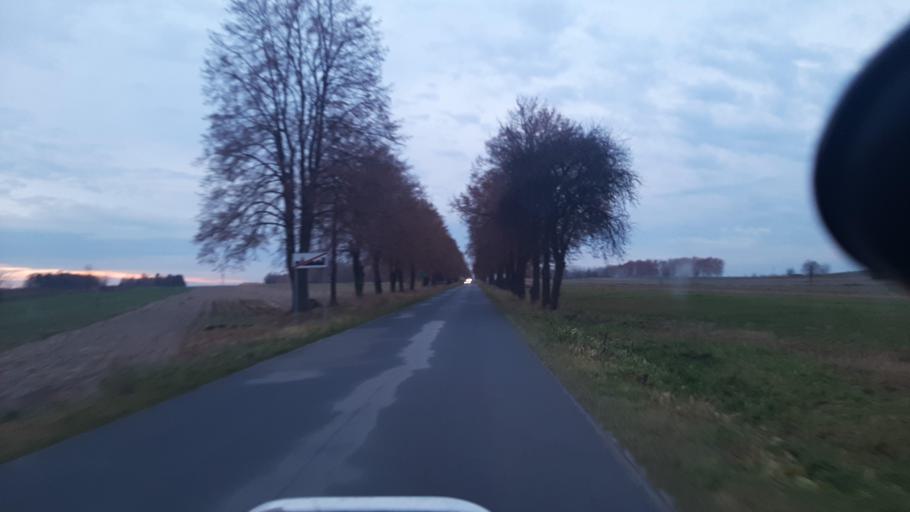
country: PL
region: Lublin Voivodeship
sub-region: Powiat lubelski
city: Garbow
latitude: 51.3818
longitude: 22.3835
